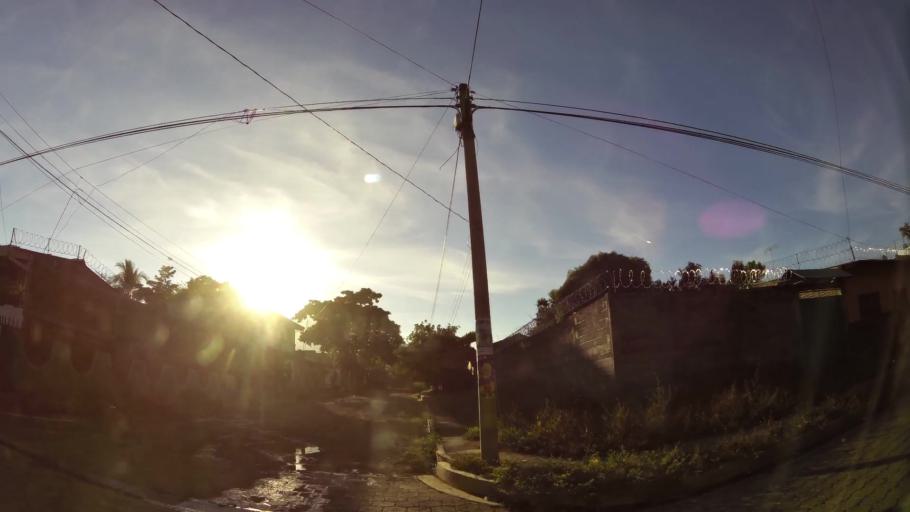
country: SV
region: San Miguel
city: San Miguel
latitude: 13.4610
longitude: -88.1675
